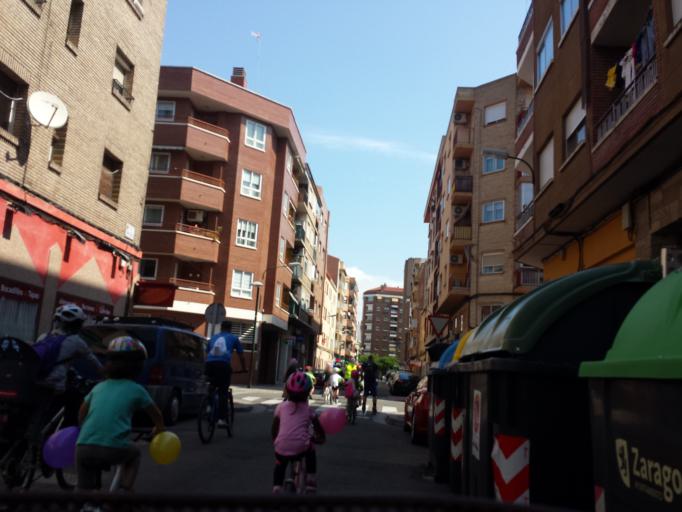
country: ES
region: Aragon
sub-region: Provincia de Zaragoza
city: Almozara
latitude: 41.6591
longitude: -0.8994
